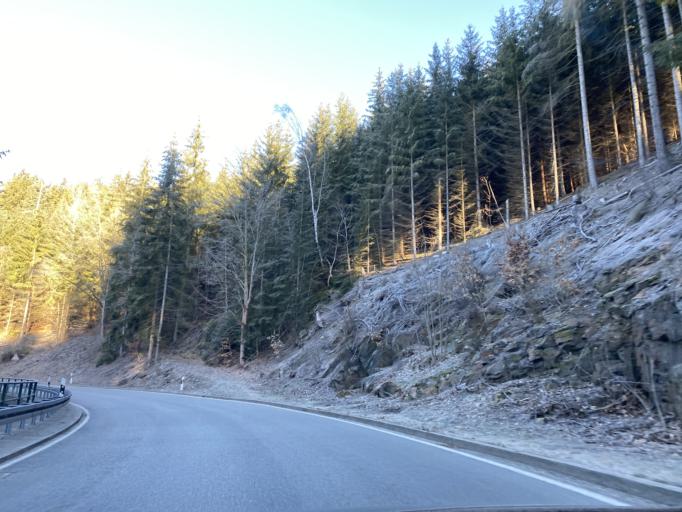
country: DE
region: Saxony
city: Thermalbad Wiesenbad
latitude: 50.6223
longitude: 13.0341
